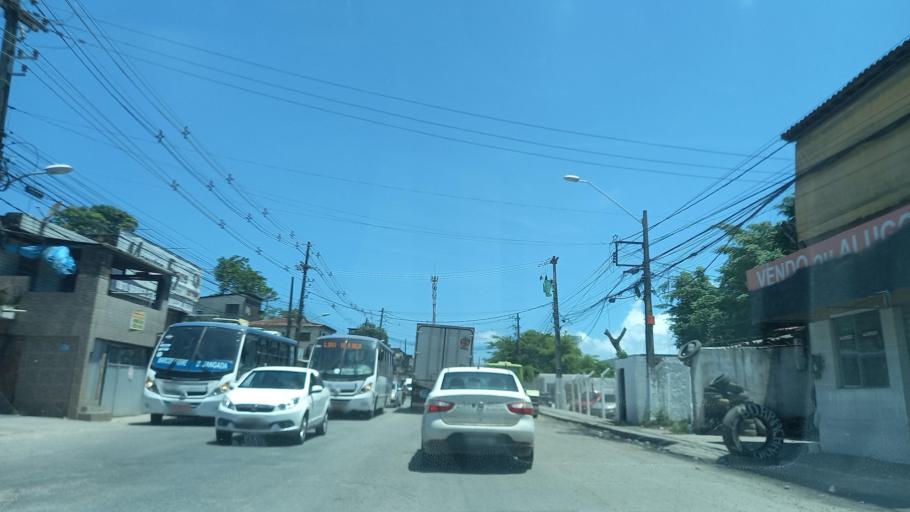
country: BR
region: Pernambuco
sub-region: Jaboatao Dos Guararapes
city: Jaboatao
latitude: -8.1549
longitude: -34.9448
